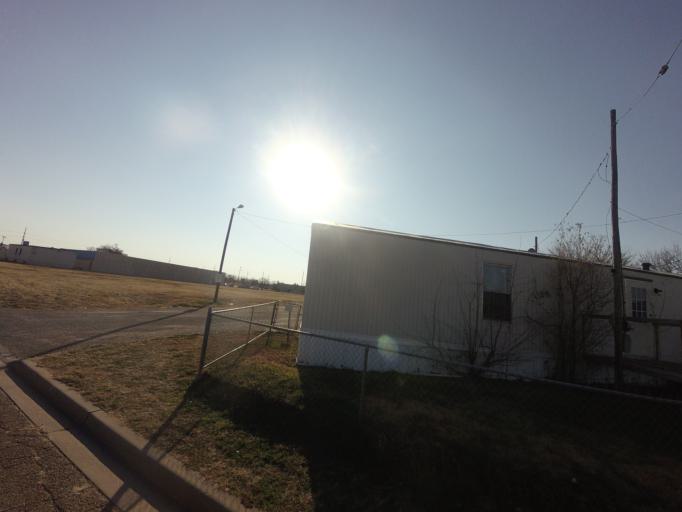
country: US
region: New Mexico
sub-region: Curry County
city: Clovis
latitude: 34.4156
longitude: -103.2084
